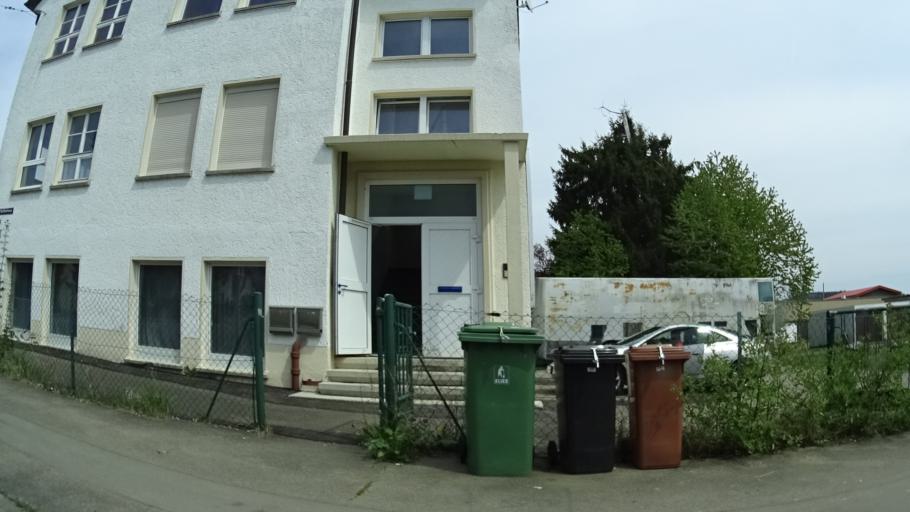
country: DE
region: Baden-Wuerttemberg
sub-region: Freiburg Region
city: Dauchingen
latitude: 48.0633
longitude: 8.5537
